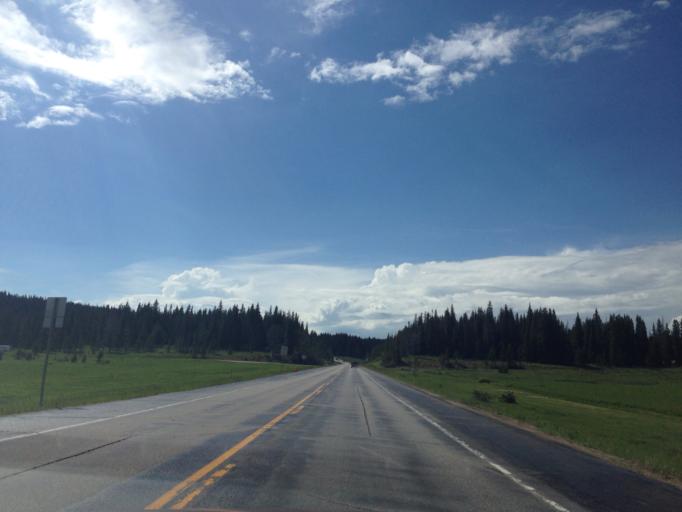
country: US
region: Colorado
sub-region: Routt County
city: Steamboat Springs
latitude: 40.3844
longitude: -106.6165
